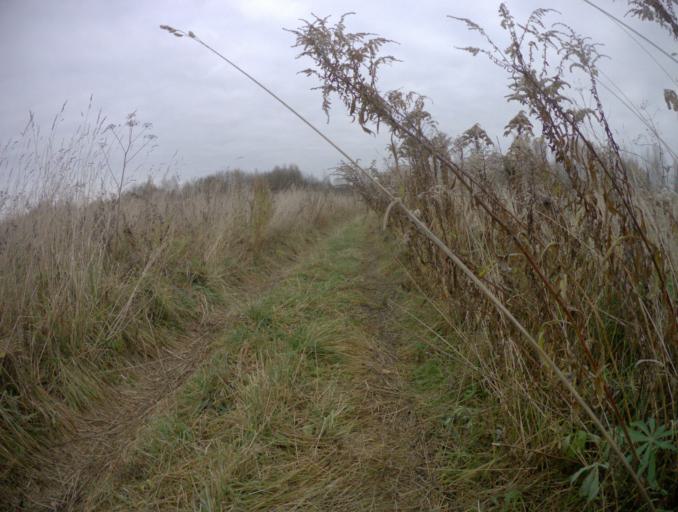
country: RU
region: Vladimir
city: Golovino
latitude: 56.0046
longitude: 40.5527
